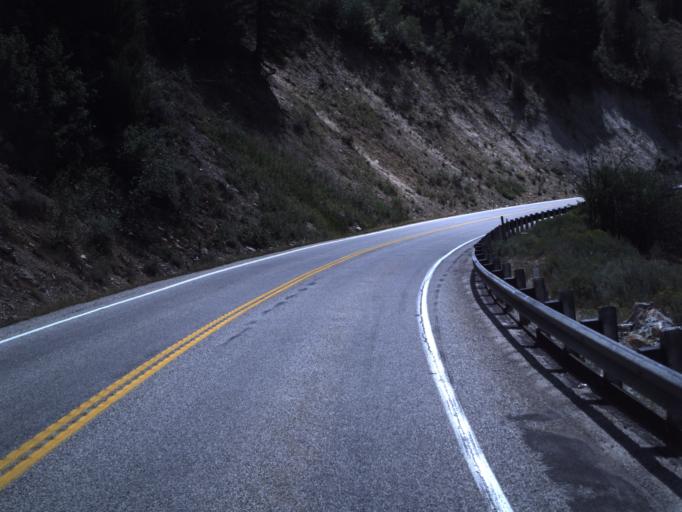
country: US
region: Utah
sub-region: Cache County
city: North Logan
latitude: 41.8262
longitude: -111.6012
